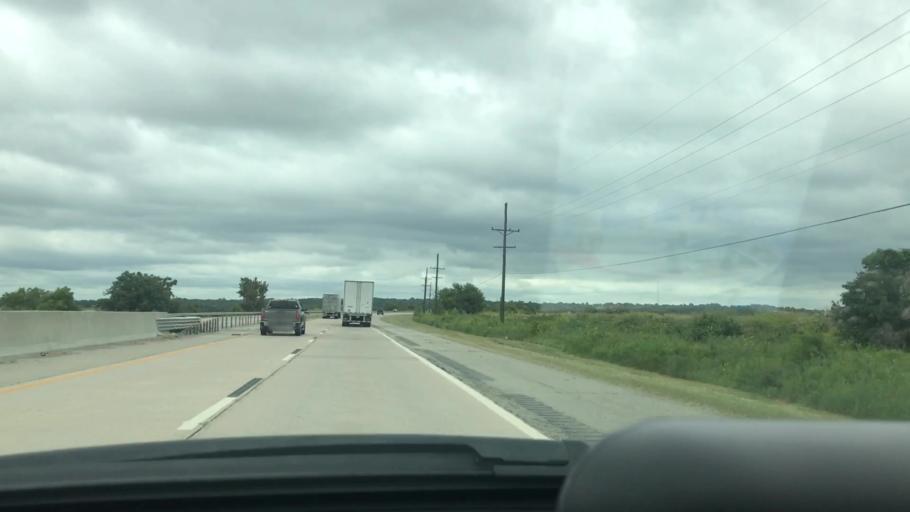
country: US
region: Oklahoma
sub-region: McIntosh County
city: Eufaula
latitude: 35.3359
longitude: -95.5867
